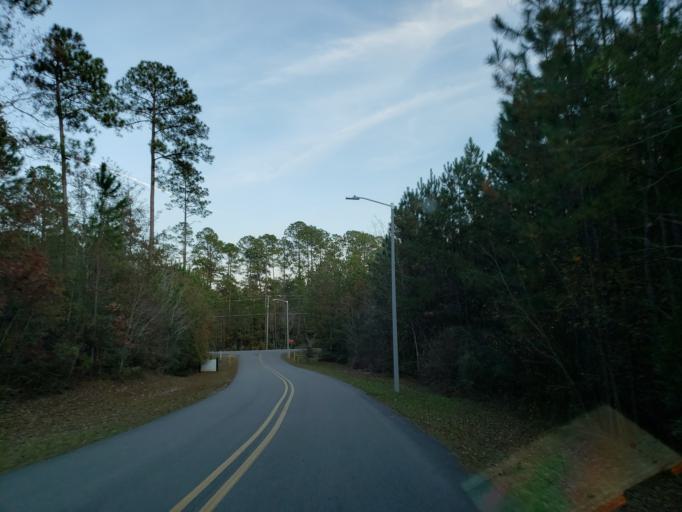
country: US
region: Mississippi
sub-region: Forrest County
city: Hattiesburg
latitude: 31.2786
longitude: -89.3095
